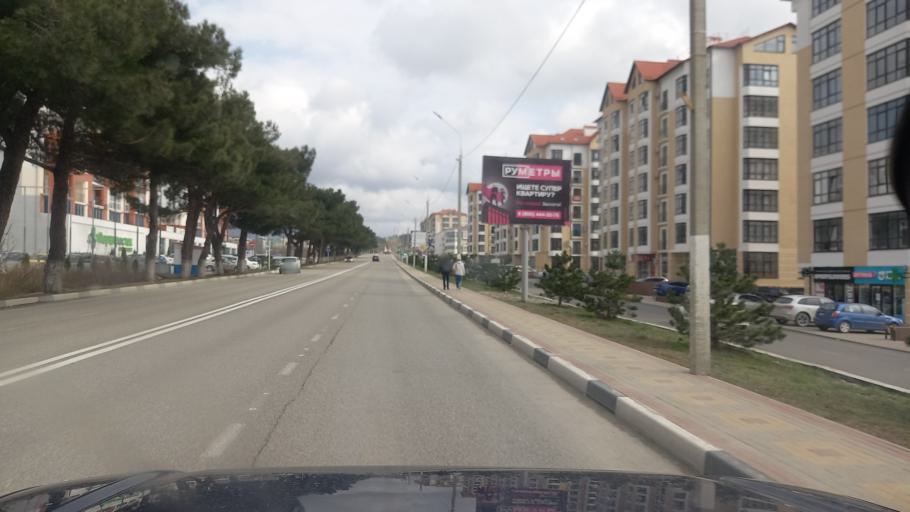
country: RU
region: Krasnodarskiy
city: Gelendzhik
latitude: 44.5570
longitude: 38.1037
